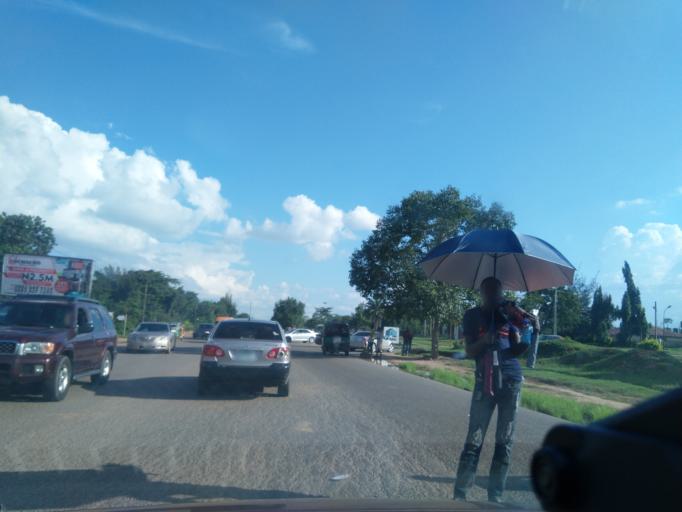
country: NG
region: Abuja Federal Capital Territory
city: Abuja
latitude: 9.0453
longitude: 7.4116
